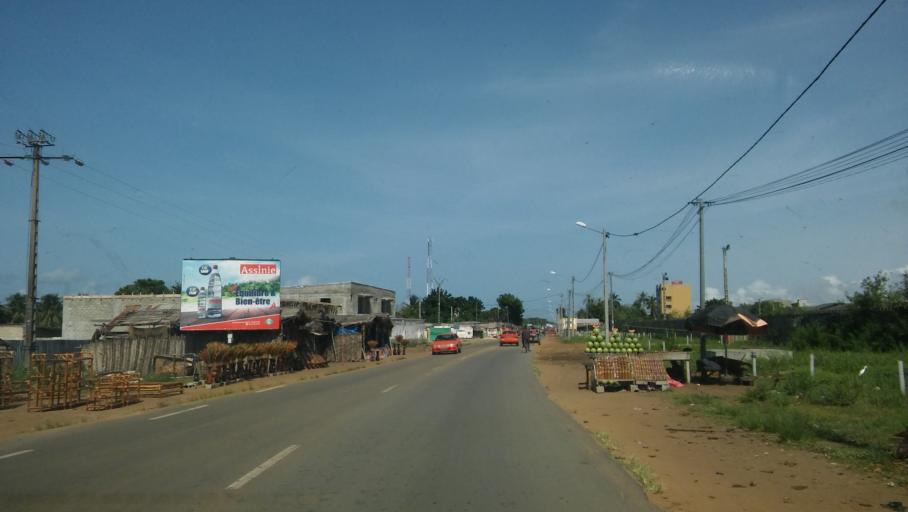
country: CI
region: Sud-Comoe
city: Grand-Bassam
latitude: 5.2103
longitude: -3.7560
